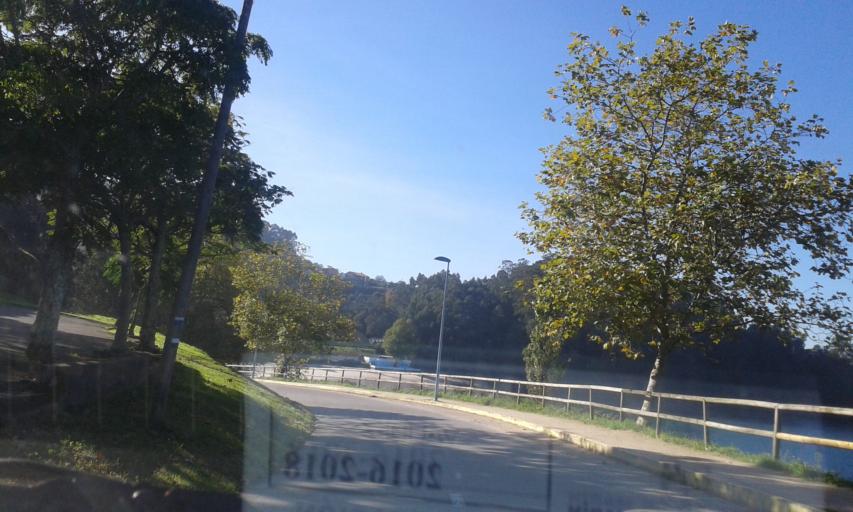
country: ES
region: Galicia
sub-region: Provincia de Pontevedra
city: Marin
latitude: 42.3878
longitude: -8.7193
